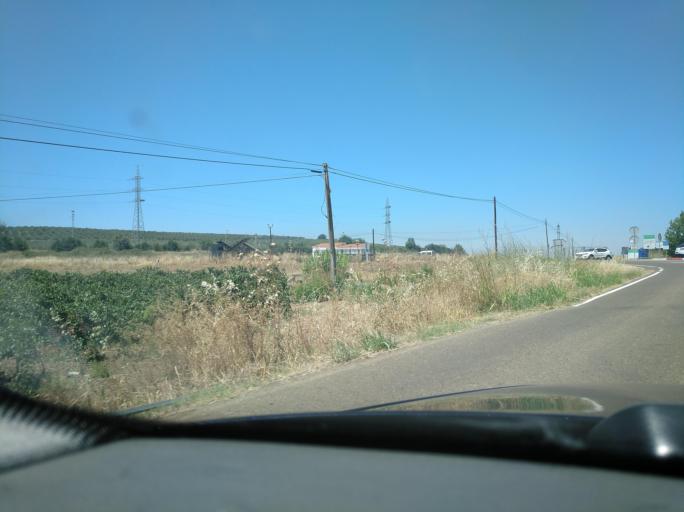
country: ES
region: Extremadura
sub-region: Provincia de Badajoz
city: Olivenza
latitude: 38.7391
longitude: -7.0647
